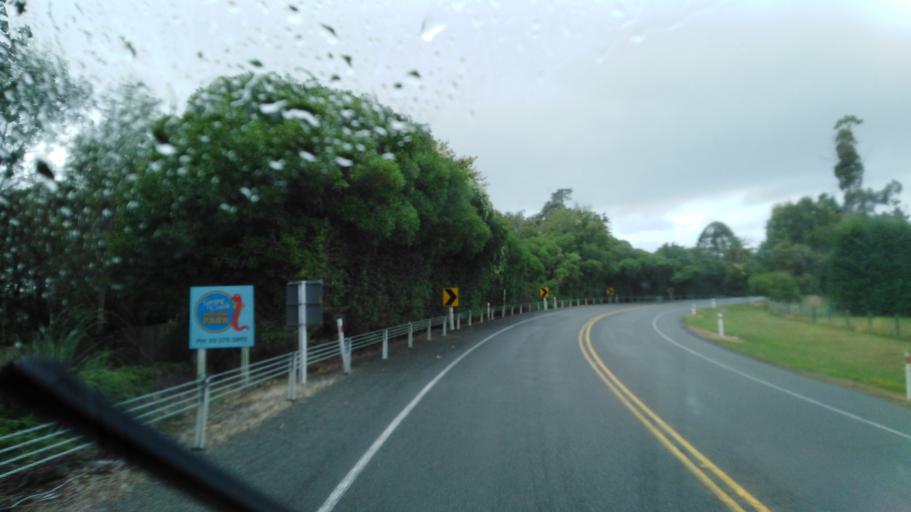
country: NZ
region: Marlborough
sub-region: Marlborough District
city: Blenheim
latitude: -41.4575
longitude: 173.9523
